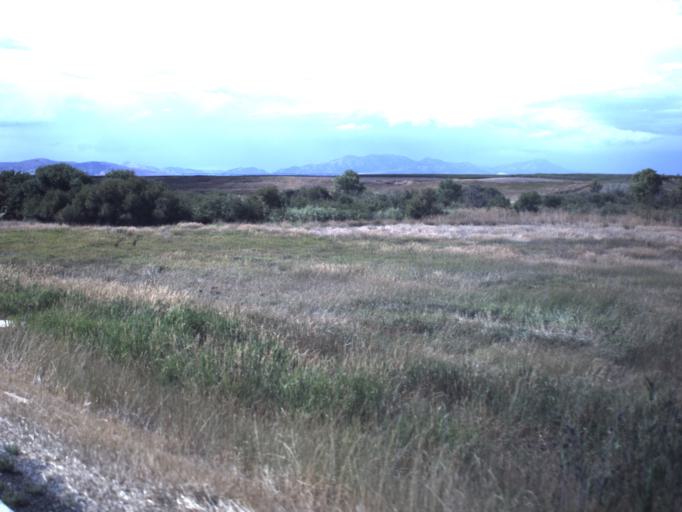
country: US
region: Utah
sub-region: Cache County
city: Richmond
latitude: 41.9238
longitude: -111.8436
